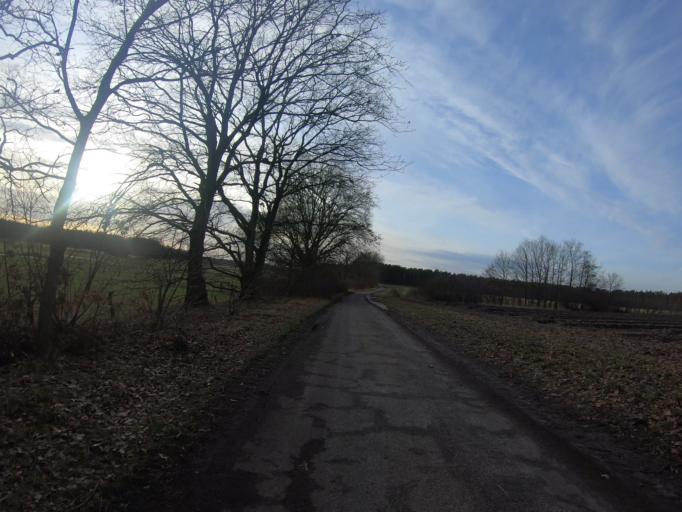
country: DE
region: Lower Saxony
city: Leiferde
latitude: 52.4936
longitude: 10.4663
